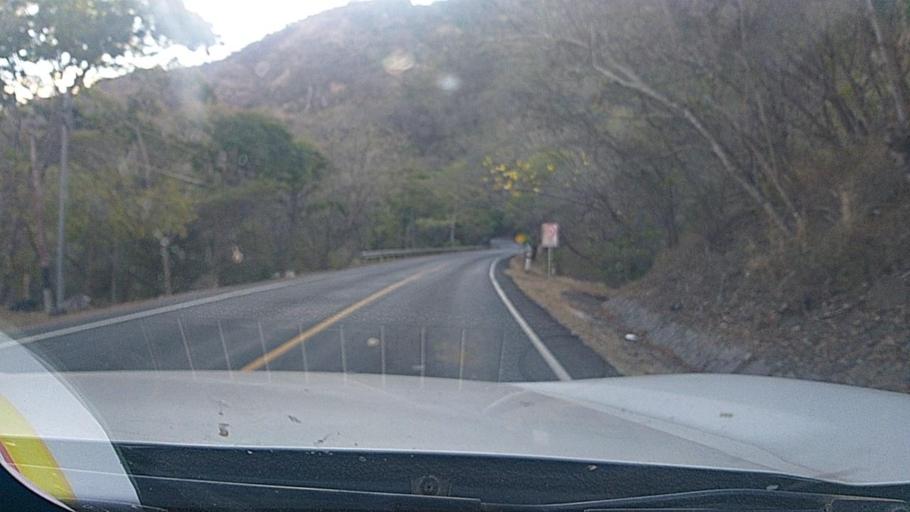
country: NI
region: Esteli
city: Condega
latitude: 13.2726
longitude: -86.3544
